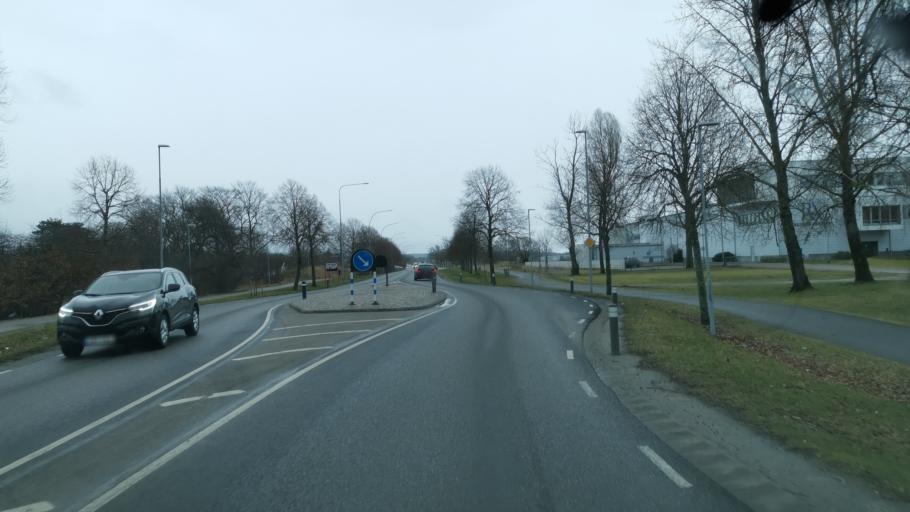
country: SE
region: Vaestra Goetaland
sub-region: Vanersborgs Kommun
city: Vanersborg
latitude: 58.3751
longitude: 12.3413
